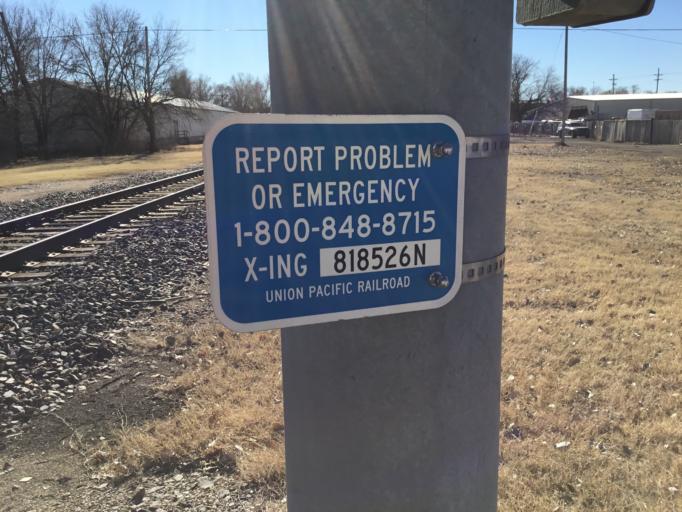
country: US
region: Kansas
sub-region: Geary County
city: Junction City
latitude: 39.0303
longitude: -96.8243
